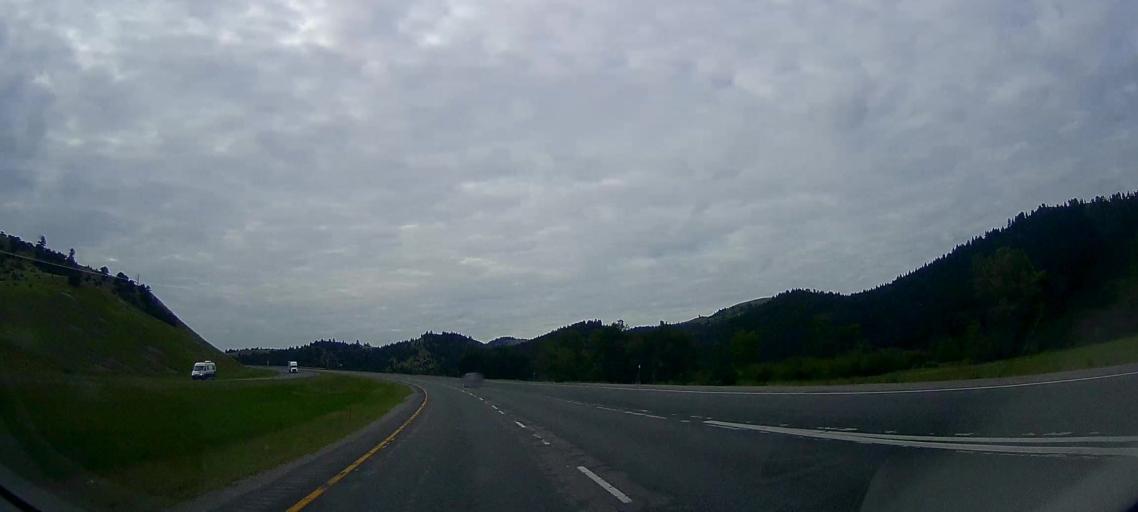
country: US
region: Montana
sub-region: Powell County
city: Deer Lodge
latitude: 46.5595
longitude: -112.8869
